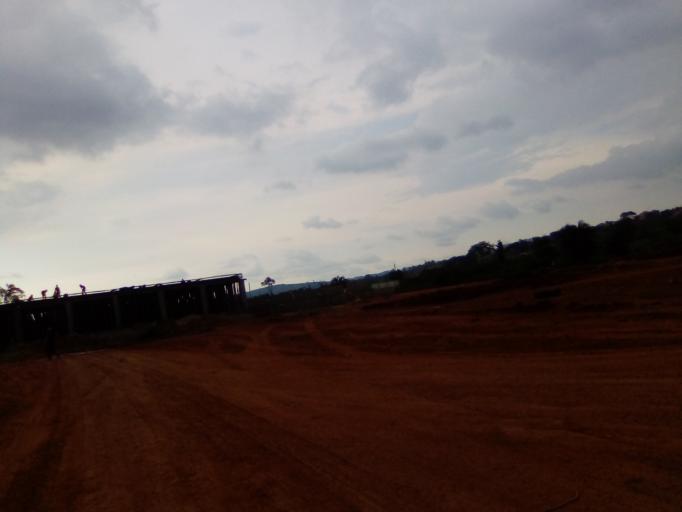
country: UG
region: Central Region
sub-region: Wakiso District
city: Kajansi
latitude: 0.1672
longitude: 32.5122
